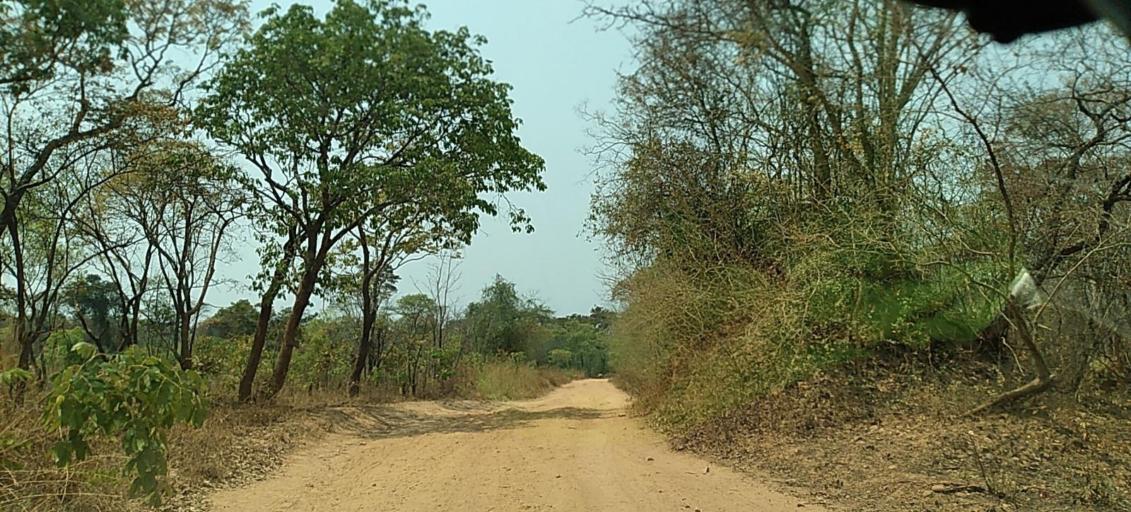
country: ZM
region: North-Western
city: Kabompo
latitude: -13.7092
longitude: 24.3261
